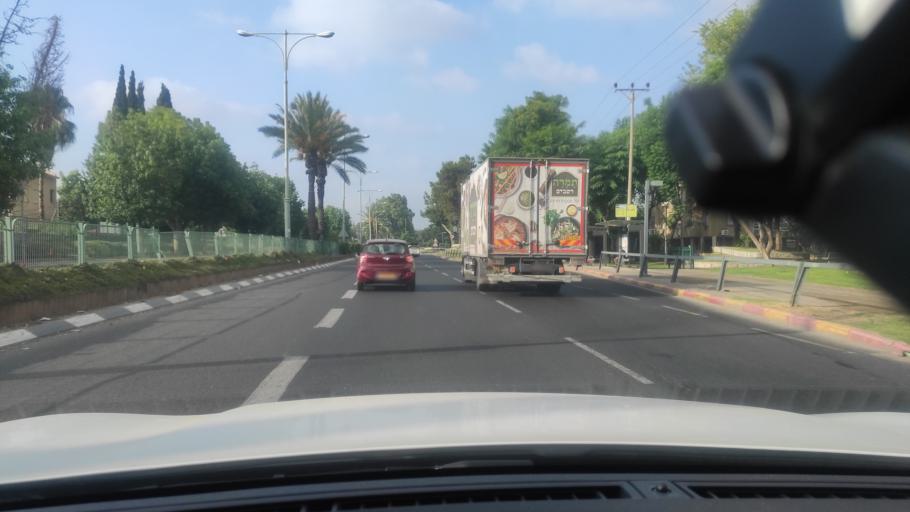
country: IL
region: Central District
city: Petah Tiqwa
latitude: 32.0908
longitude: 34.9019
